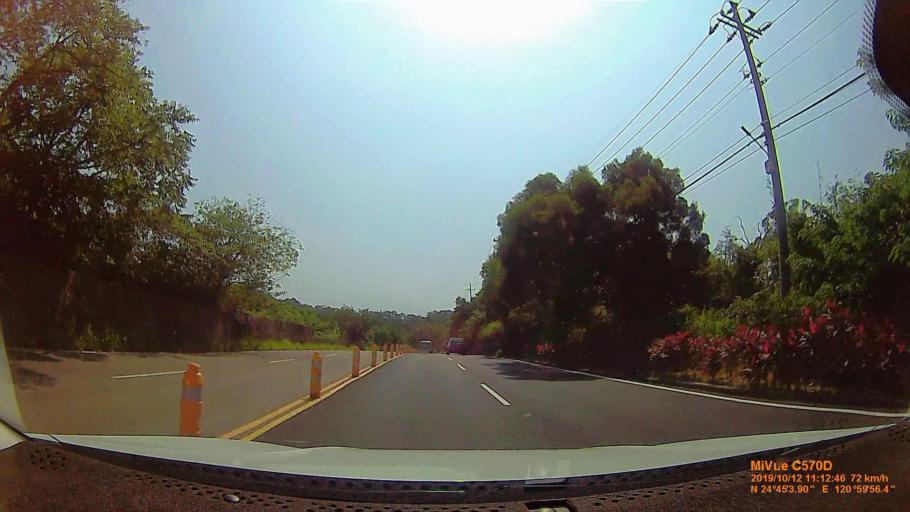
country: TW
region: Taiwan
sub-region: Hsinchu
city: Hsinchu
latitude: 24.7510
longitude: 120.9993
